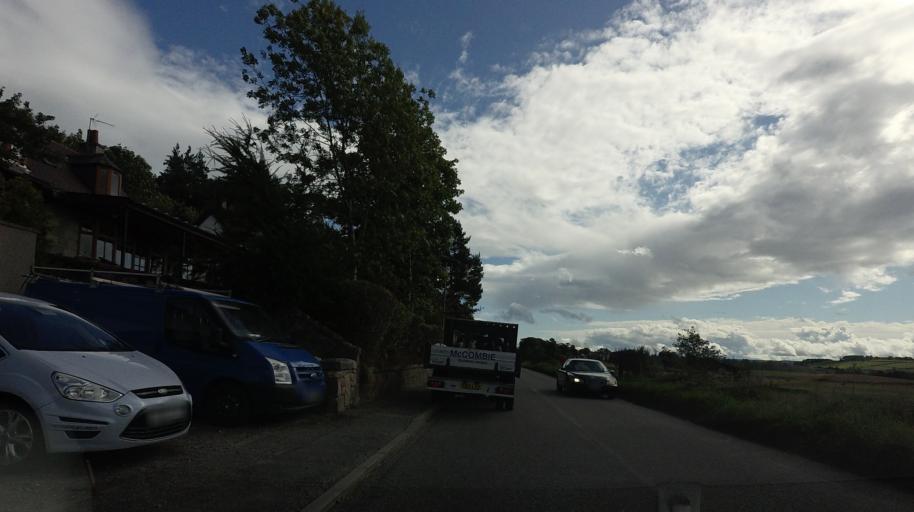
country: GB
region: Scotland
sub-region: Aberdeenshire
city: Torphins
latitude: 57.1088
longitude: -2.6321
